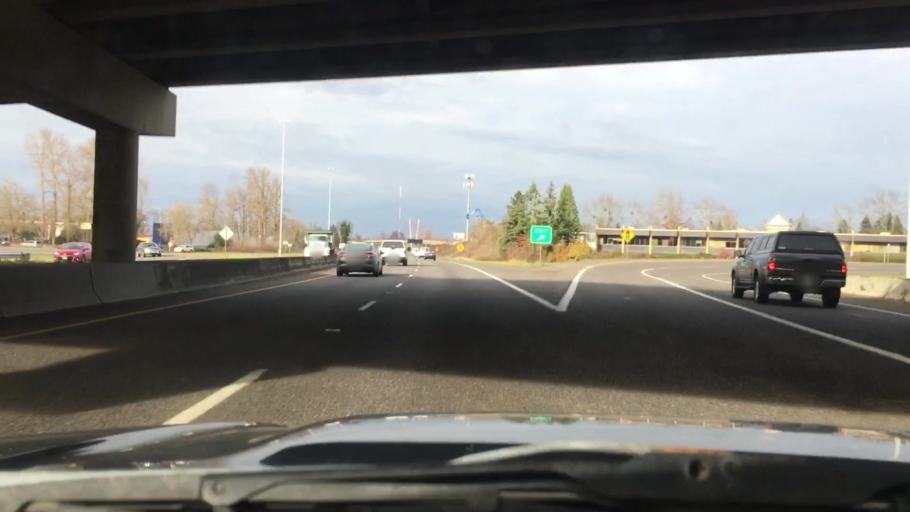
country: US
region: Oregon
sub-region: Lane County
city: Eugene
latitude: 44.0702
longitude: -123.1018
